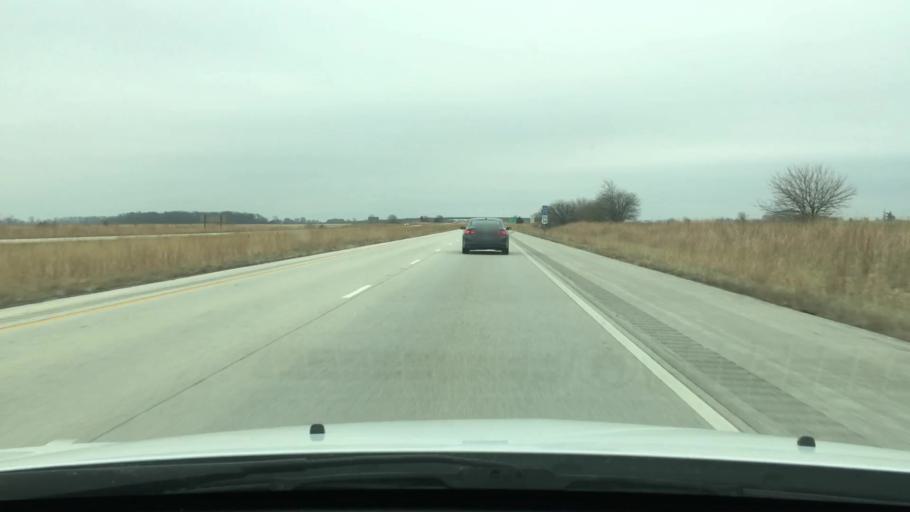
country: US
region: Illinois
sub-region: Sangamon County
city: New Berlin
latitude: 39.7401
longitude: -89.9135
